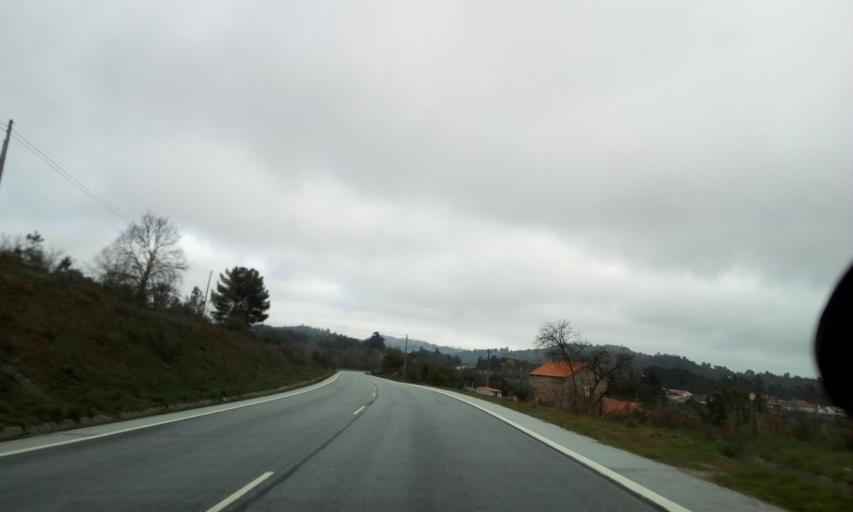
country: PT
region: Guarda
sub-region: Fornos de Algodres
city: Fornos de Algodres
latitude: 40.6311
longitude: -7.5021
